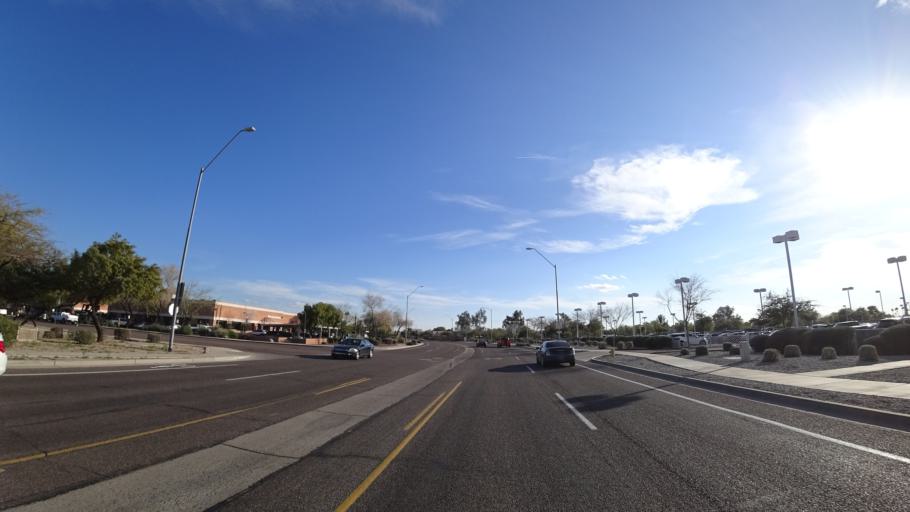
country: US
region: Arizona
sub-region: Maricopa County
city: Sun City
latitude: 33.6357
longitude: -112.2530
